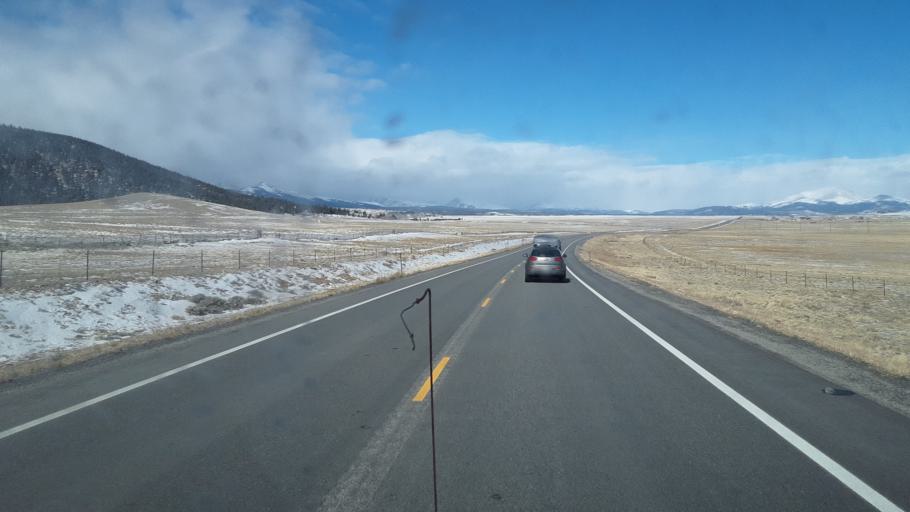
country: US
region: Colorado
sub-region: Park County
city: Fairplay
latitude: 39.0953
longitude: -105.9876
